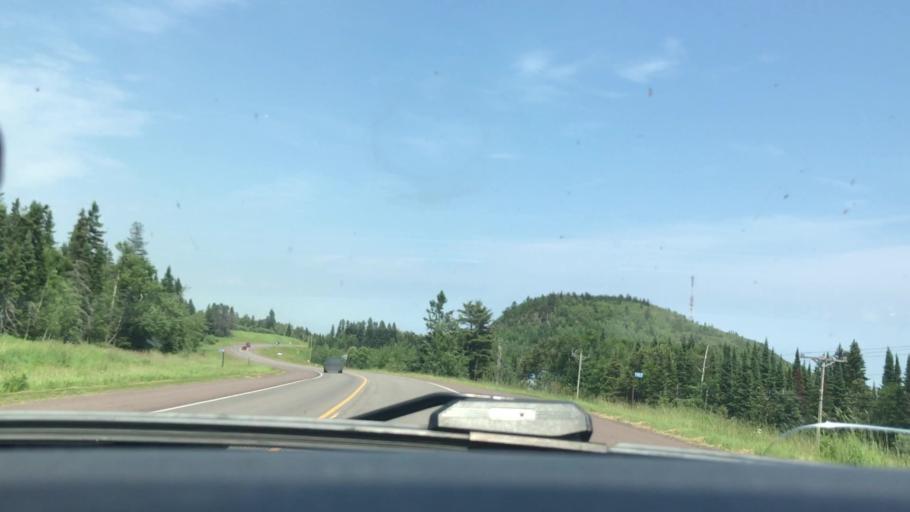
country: US
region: Minnesota
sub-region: Lake County
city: Silver Bay
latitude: 47.3153
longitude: -91.2257
